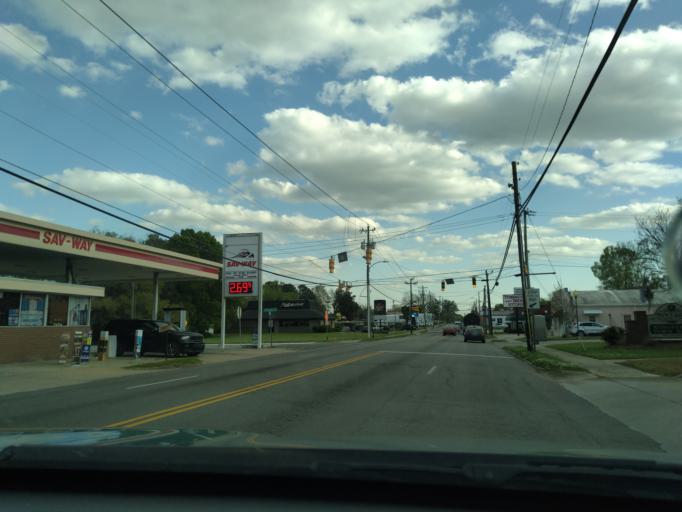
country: US
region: South Carolina
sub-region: Williamsburg County
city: Kingstree
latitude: 33.6674
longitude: -79.8348
